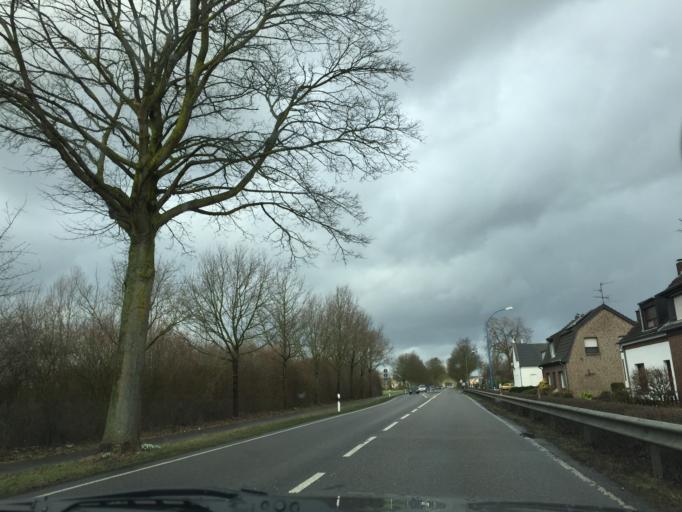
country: DE
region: North Rhine-Westphalia
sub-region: Regierungsbezirk Dusseldorf
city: Kleve
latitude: 51.7581
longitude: 6.1515
